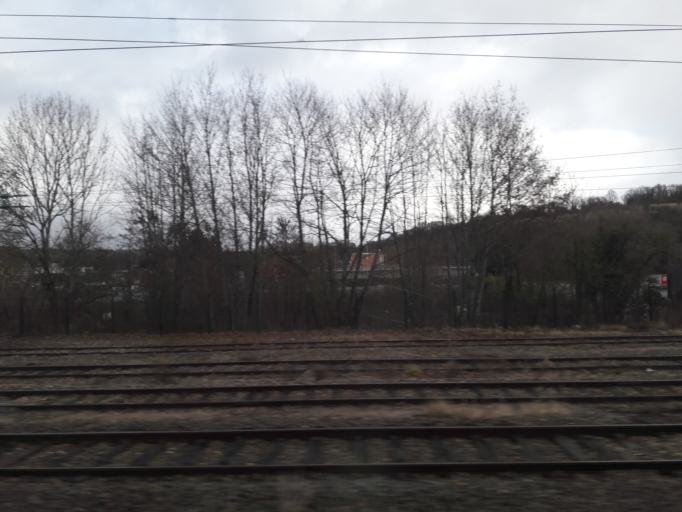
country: FR
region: Franche-Comte
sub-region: Territoire de Belfort
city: Belfort
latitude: 47.6246
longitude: 6.8589
